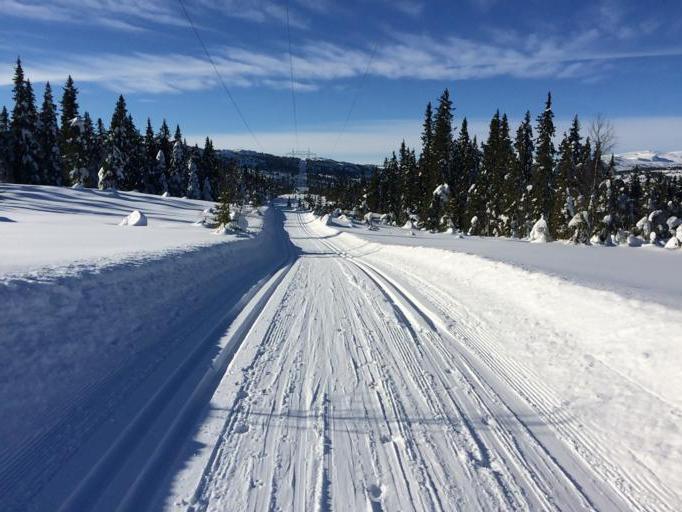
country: NO
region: Oppland
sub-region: Gausdal
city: Segalstad bru
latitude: 61.3189
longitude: 10.0914
